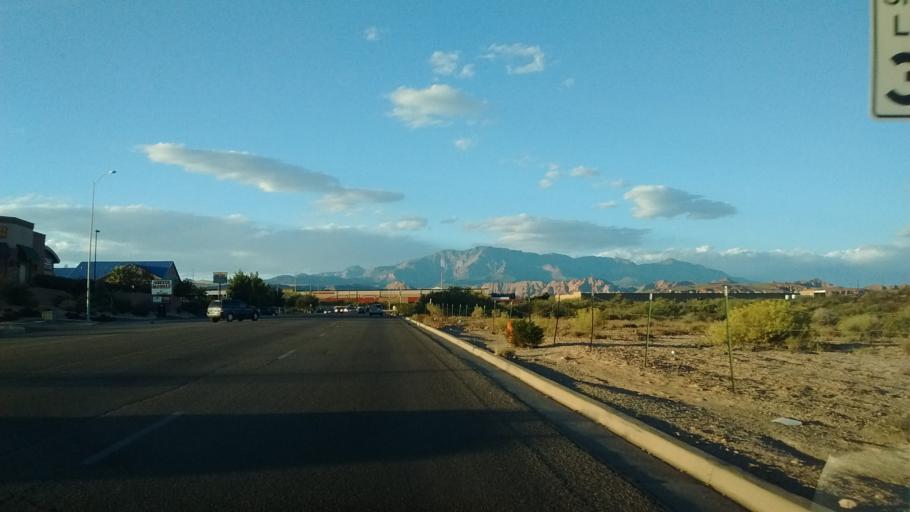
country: US
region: Utah
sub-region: Washington County
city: Washington
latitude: 37.1206
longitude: -113.5207
